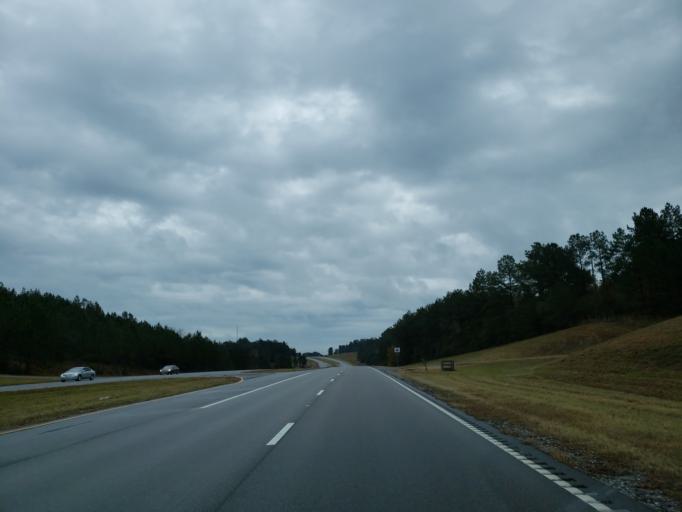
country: US
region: Mississippi
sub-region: Wayne County
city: Waynesboro
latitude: 31.6879
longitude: -88.7073
